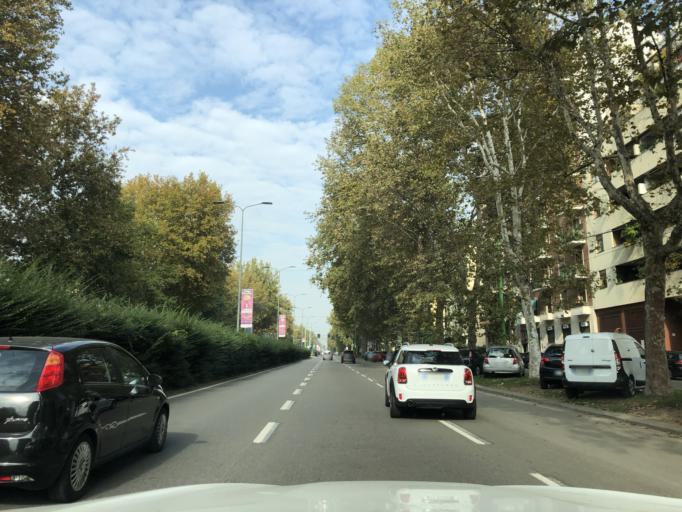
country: IT
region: Lombardy
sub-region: Citta metropolitana di Milano
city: Bresso
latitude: 45.5048
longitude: 9.1998
